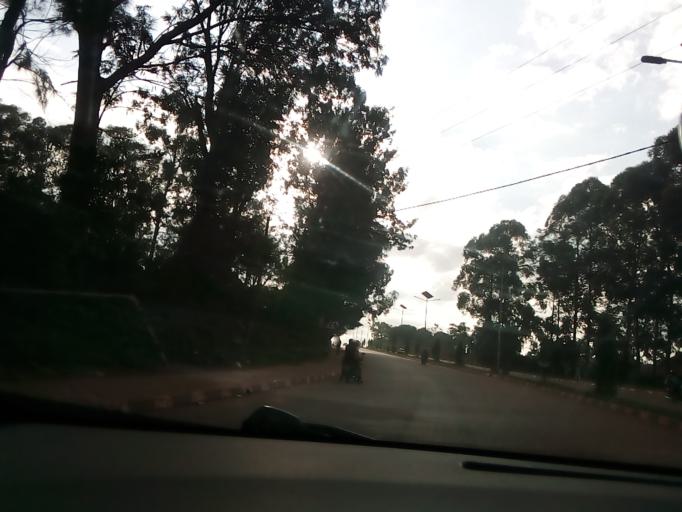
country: UG
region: Central Region
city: Masaka
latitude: -0.3494
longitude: 31.7349
